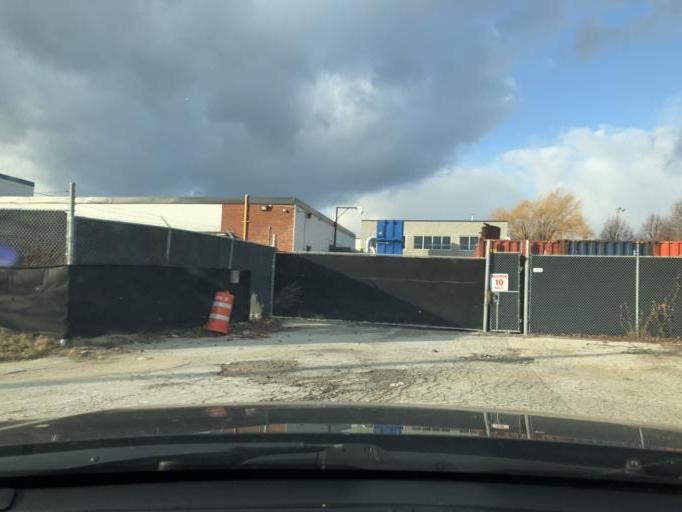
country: CA
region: Ontario
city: Scarborough
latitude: 43.7709
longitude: -79.2910
